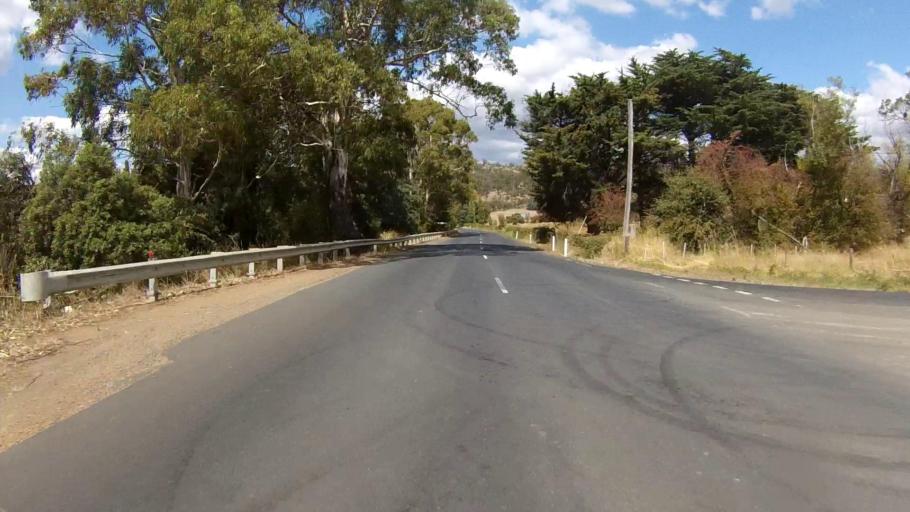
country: AU
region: Tasmania
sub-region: Derwent Valley
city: New Norfolk
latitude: -42.7719
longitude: 147.0272
